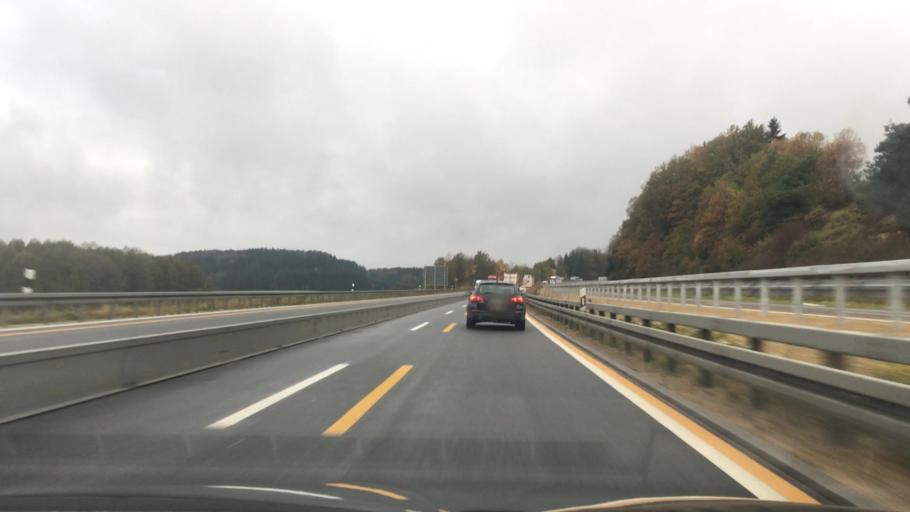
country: DE
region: Bavaria
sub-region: Upper Palatinate
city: Deining
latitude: 49.2847
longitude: 11.5680
